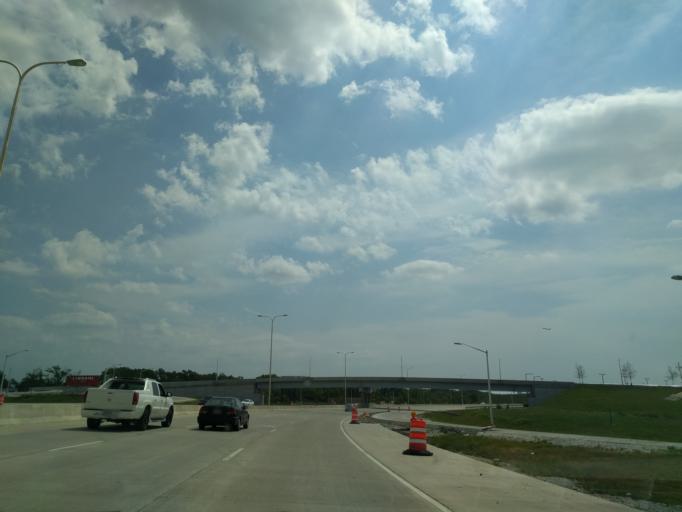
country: US
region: Illinois
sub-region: Cook County
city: Rosemont
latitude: 41.9904
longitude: -87.8811
